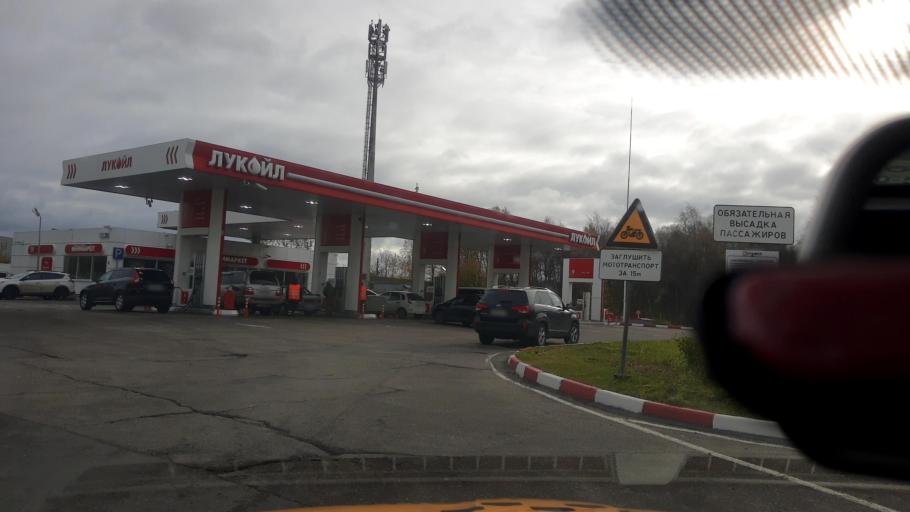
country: RU
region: Moskovskaya
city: Zhavoronki
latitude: 55.6126
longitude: 37.0801
